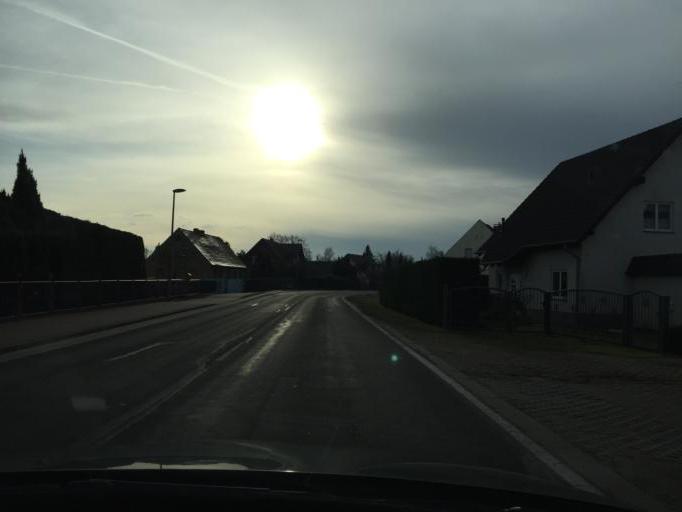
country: DE
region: Brandenburg
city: Peitz
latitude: 51.8646
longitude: 14.4168
